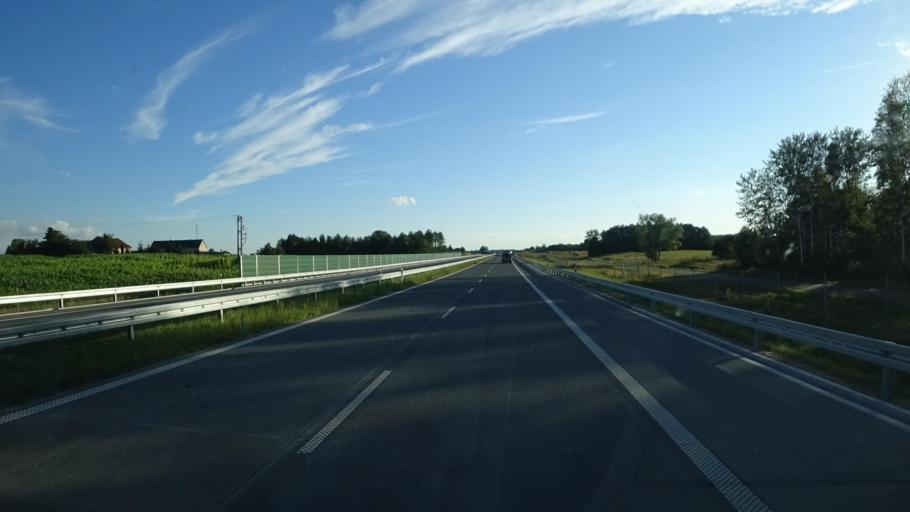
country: PL
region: Podlasie
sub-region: Powiat suwalski
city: Raczki
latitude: 53.9160
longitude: 22.7324
